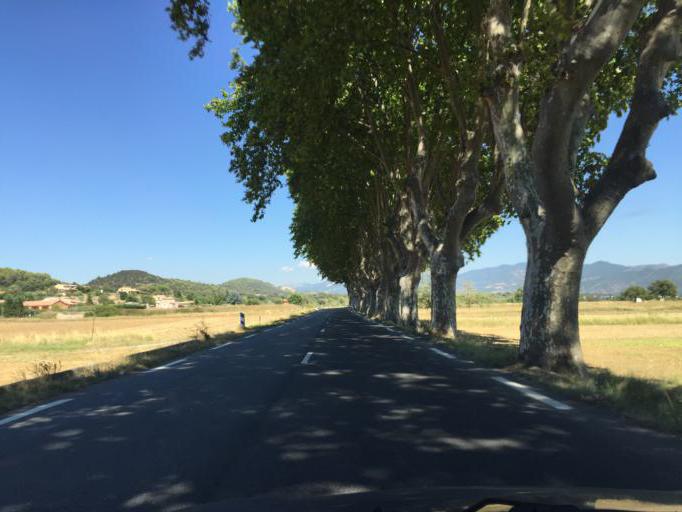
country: FR
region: Provence-Alpes-Cote d'Azur
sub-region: Departement des Alpes-de-Haute-Provence
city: Peyruis
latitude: 44.0384
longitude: 5.9502
